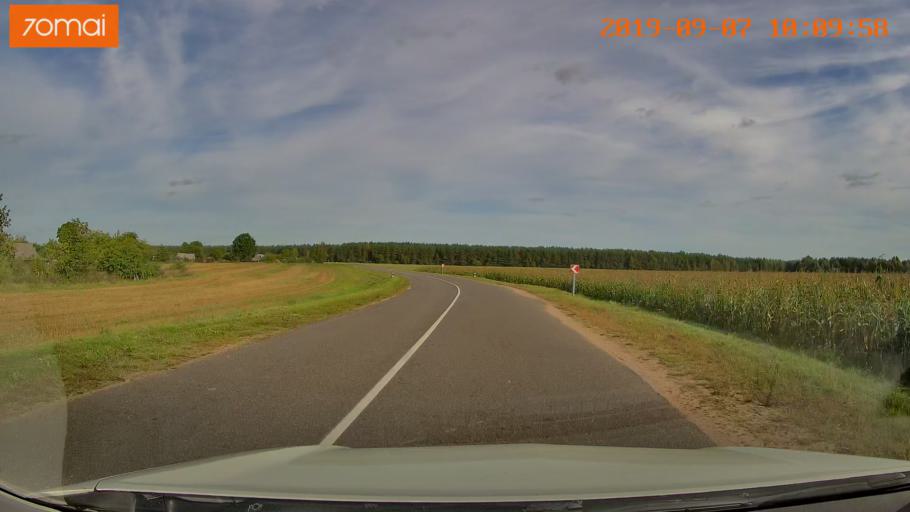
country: BY
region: Grodnenskaya
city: Voranava
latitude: 54.1018
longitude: 25.3717
